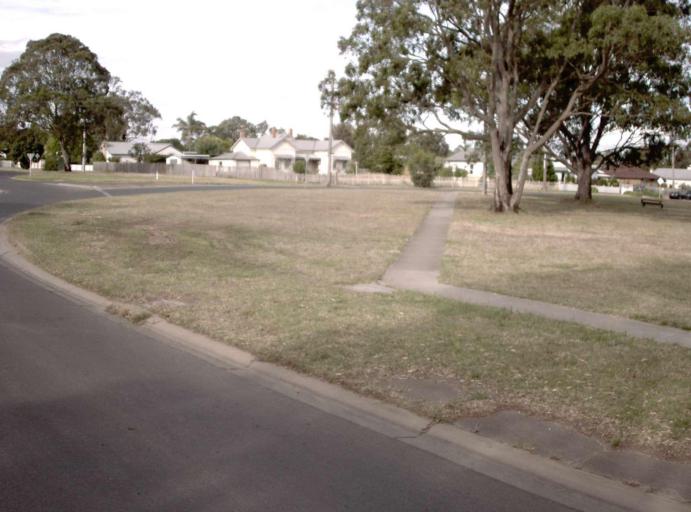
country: AU
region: Victoria
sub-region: Wellington
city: Heyfield
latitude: -37.9790
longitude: 146.7842
